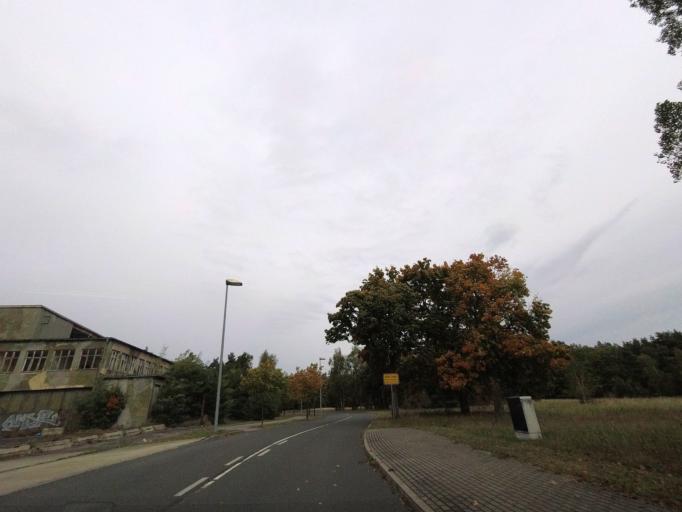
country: DE
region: Brandenburg
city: Niedergorsdorf
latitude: 52.0031
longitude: 13.0006
